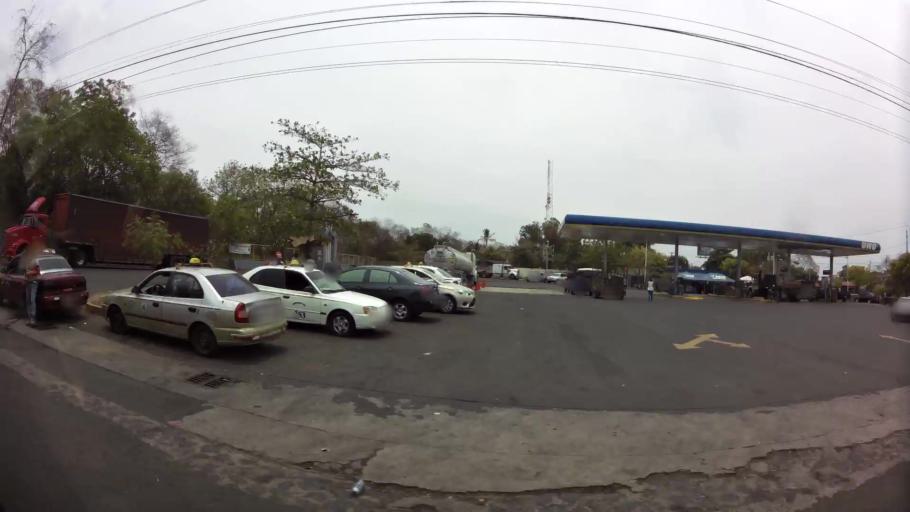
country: NI
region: Leon
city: Leon
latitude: 12.4209
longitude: -86.8710
